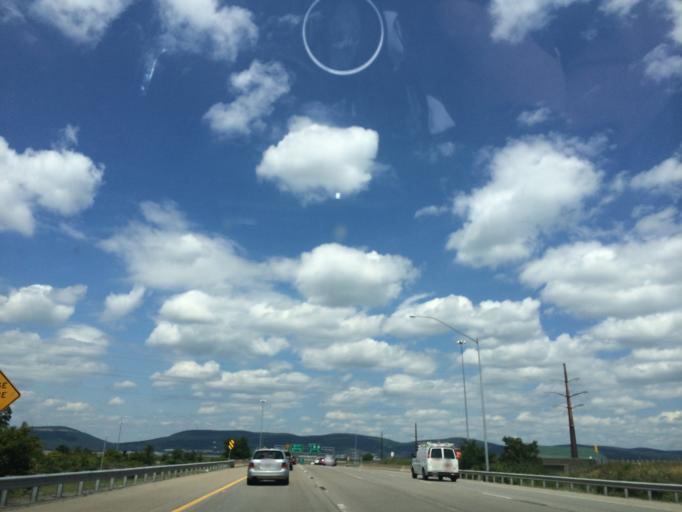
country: US
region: Pennsylvania
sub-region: Lackawanna County
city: Dunmore
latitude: 41.4184
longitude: -75.6030
